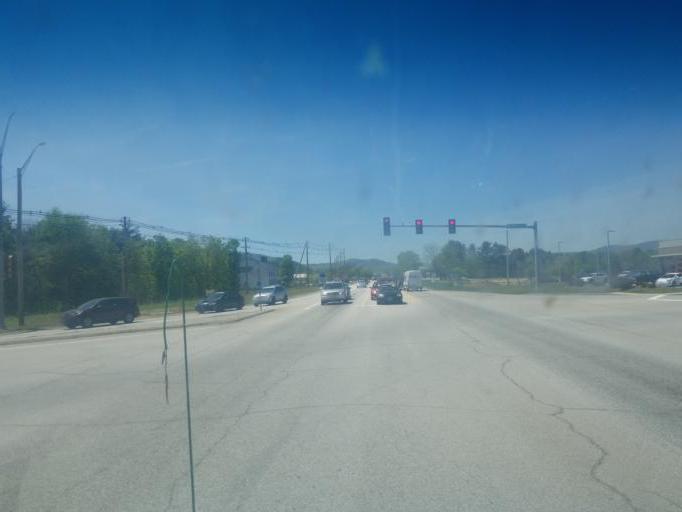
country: US
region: New Hampshire
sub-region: Grafton County
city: Plymouth
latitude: 43.7708
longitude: -71.7217
